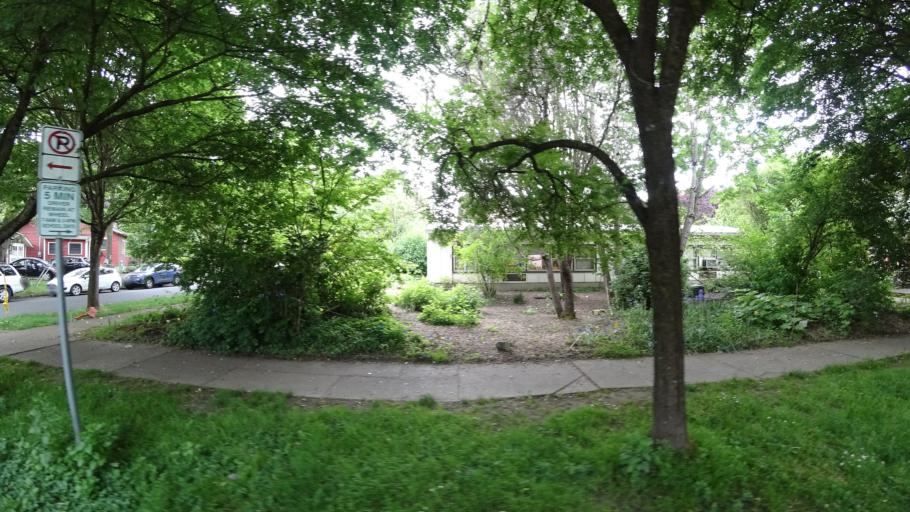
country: US
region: Oregon
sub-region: Multnomah County
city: Portland
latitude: 45.5064
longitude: -122.6506
